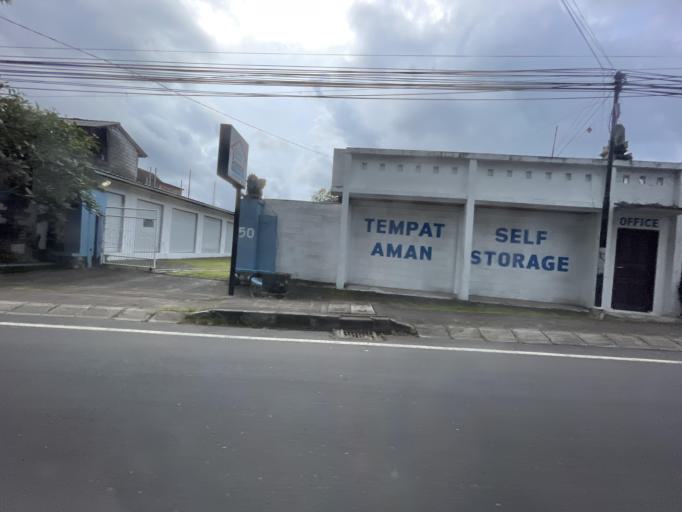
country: ID
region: Bali
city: Banjar Sedang
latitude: -8.5562
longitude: 115.2723
